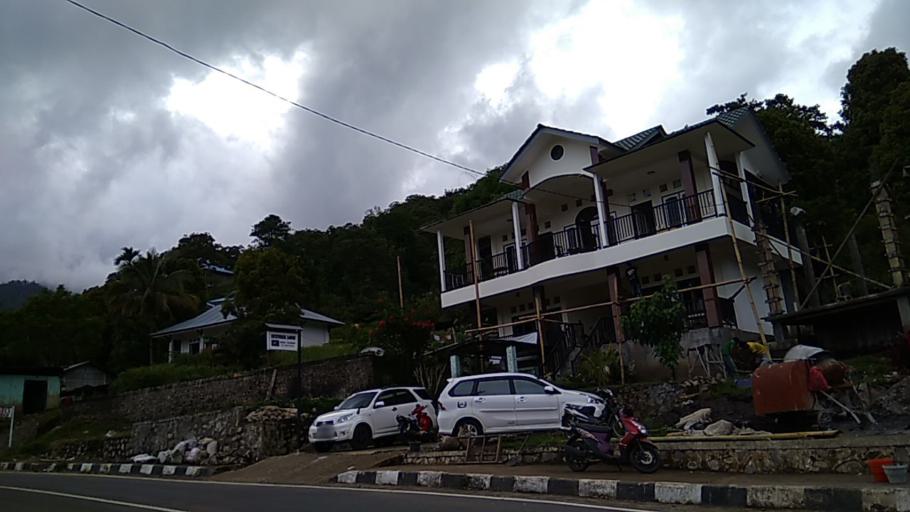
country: ID
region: East Nusa Tenggara
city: Koanara
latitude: -8.7496
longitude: 121.8494
